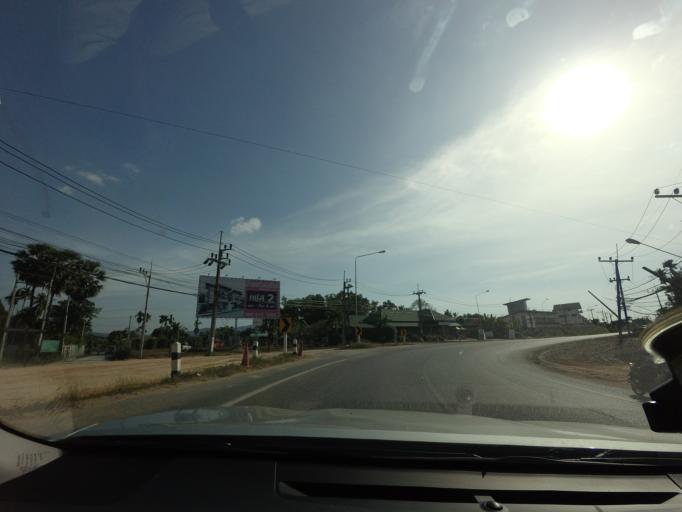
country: TH
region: Phuket
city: Thalang
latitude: 8.0215
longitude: 98.3276
